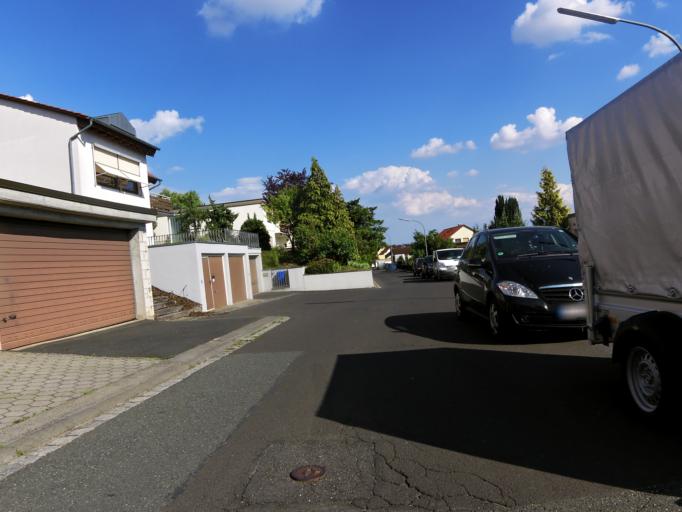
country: DE
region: Bavaria
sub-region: Regierungsbezirk Unterfranken
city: Rimpar
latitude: 49.8271
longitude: 9.9600
